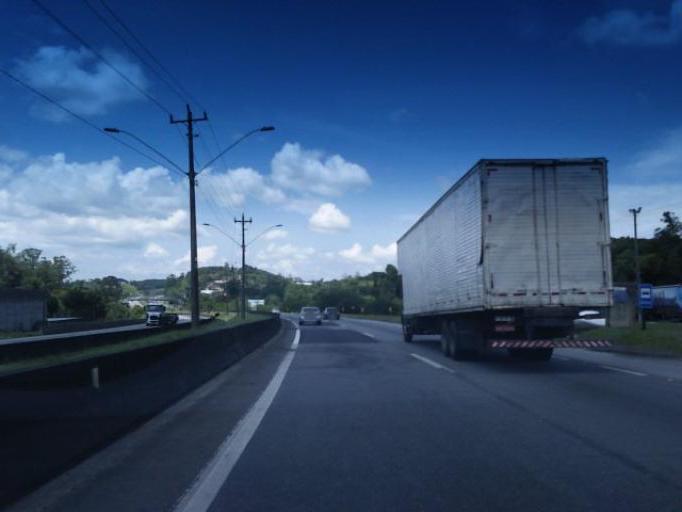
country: BR
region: Sao Paulo
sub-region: Sao Lourenco Da Serra
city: Sao Lourenco da Serra
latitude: -23.8911
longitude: -46.9827
